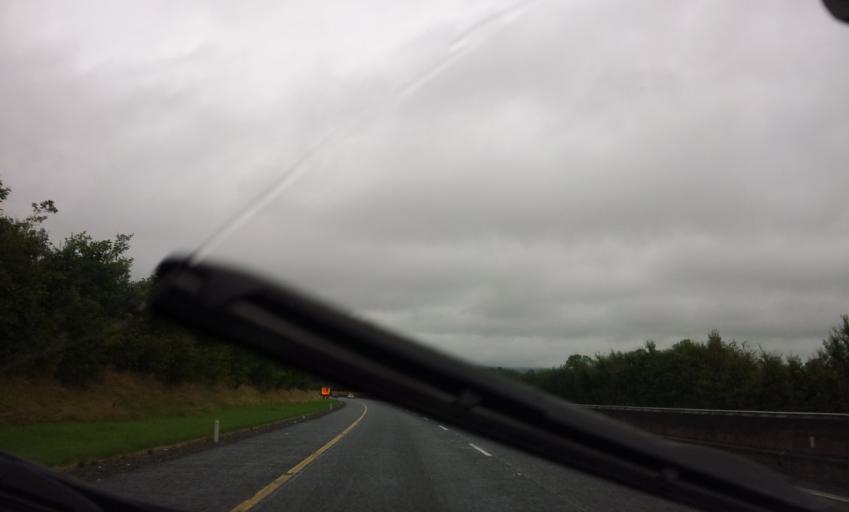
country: IE
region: Munster
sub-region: County Cork
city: Fermoy
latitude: 52.1302
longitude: -8.2599
